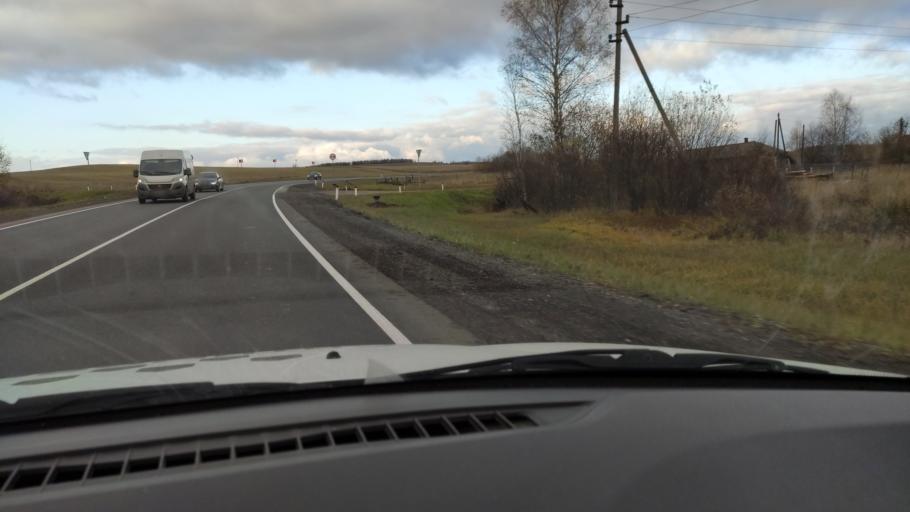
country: RU
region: Kirov
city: Belaya Kholunitsa
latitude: 58.8902
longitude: 50.8757
